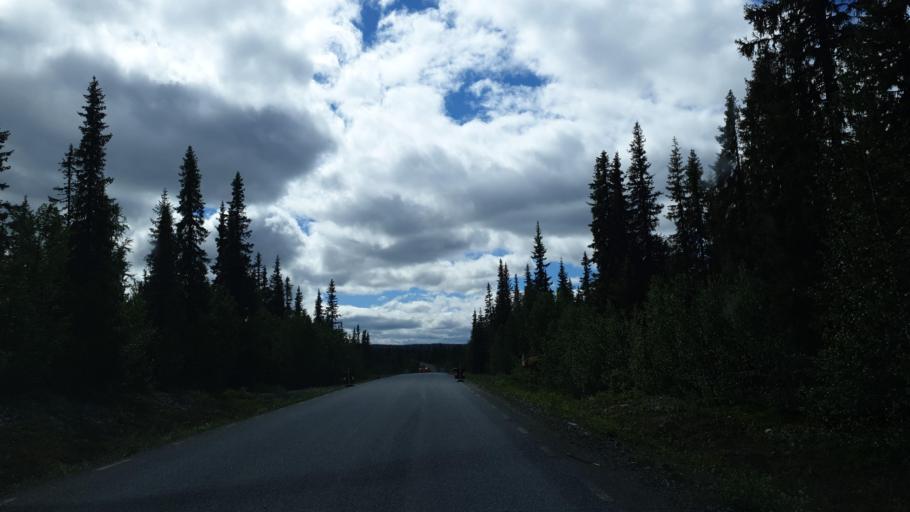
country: SE
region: Vaesterbotten
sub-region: Vilhelmina Kommun
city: Sjoberg
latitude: 65.1579
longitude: 15.8654
